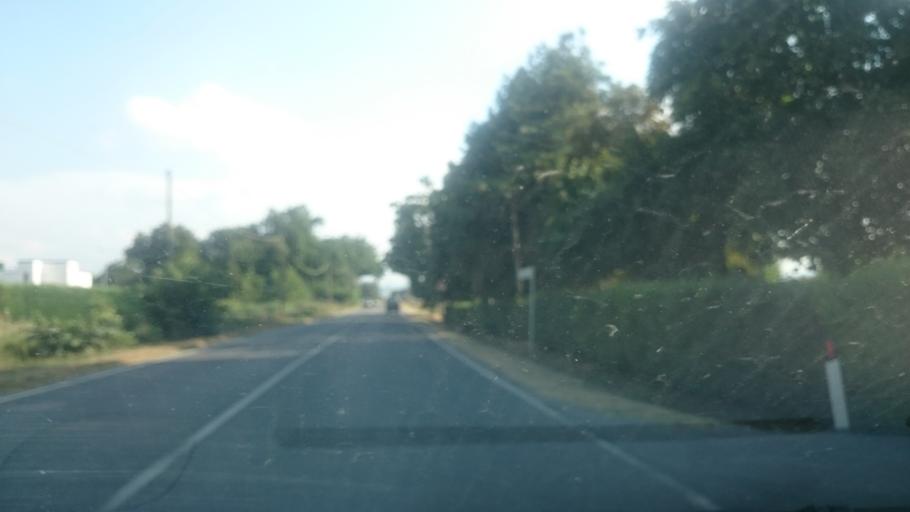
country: IT
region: Emilia-Romagna
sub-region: Provincia di Reggio Emilia
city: Rubiera
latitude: 44.6330
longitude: 10.7780
